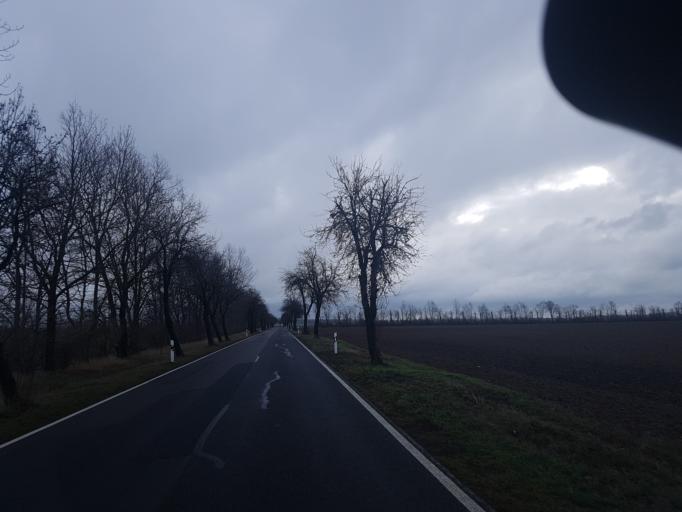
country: DE
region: Brandenburg
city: Muhlberg
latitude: 51.4172
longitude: 13.2338
